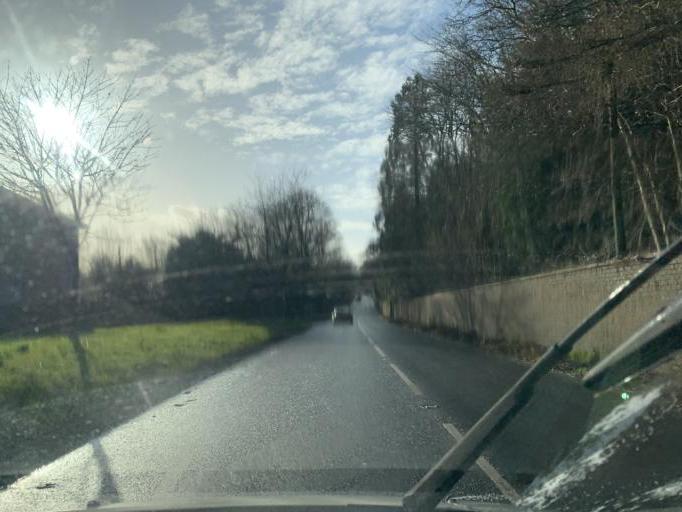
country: GB
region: England
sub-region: Wiltshire
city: Wilton
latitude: 51.0787
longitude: -1.8482
